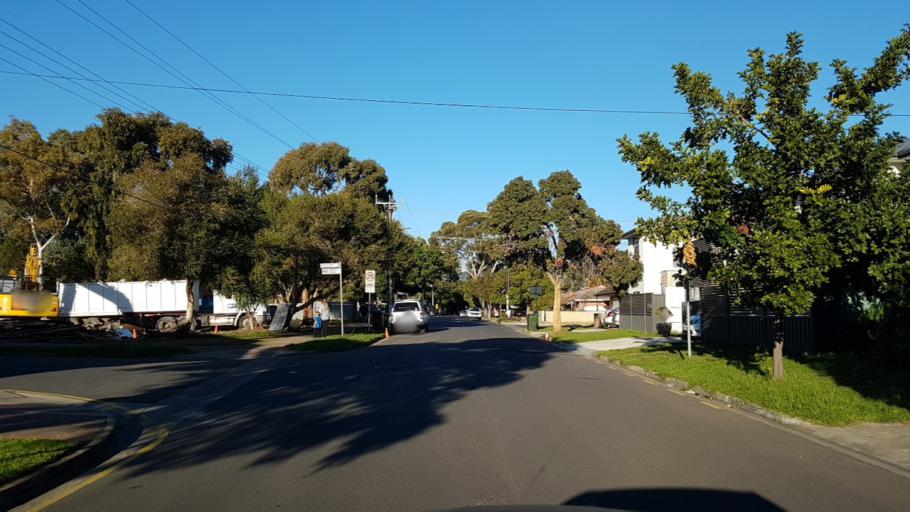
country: AU
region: South Australia
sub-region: Campbelltown
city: Hectorville
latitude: -34.8825
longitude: 138.6517
